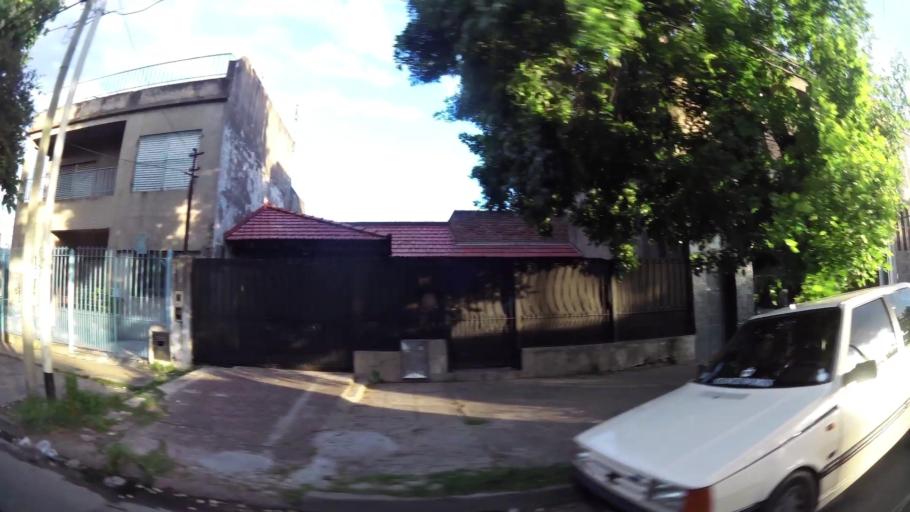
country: AR
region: Buenos Aires
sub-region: Partido de Avellaneda
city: Avellaneda
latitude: -34.7062
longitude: -58.3373
